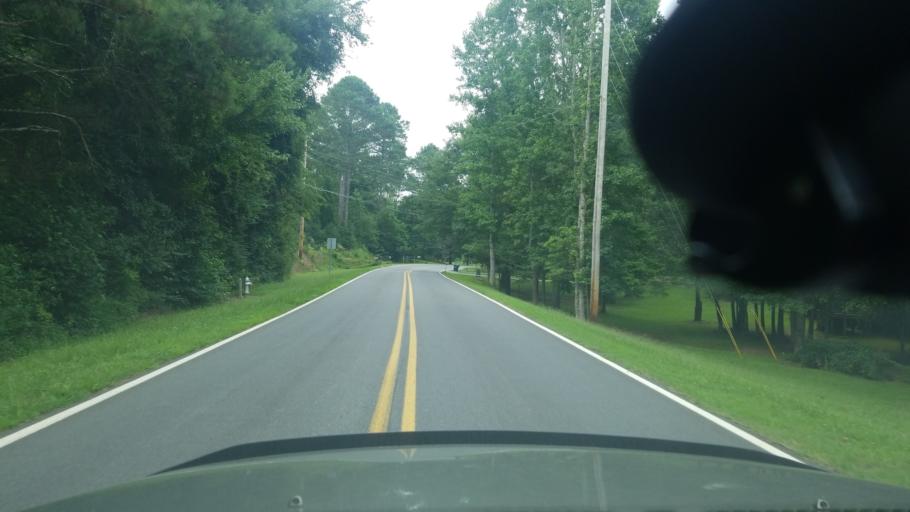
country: US
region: Georgia
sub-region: Dawson County
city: Dawsonville
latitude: 34.3274
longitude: -84.1821
